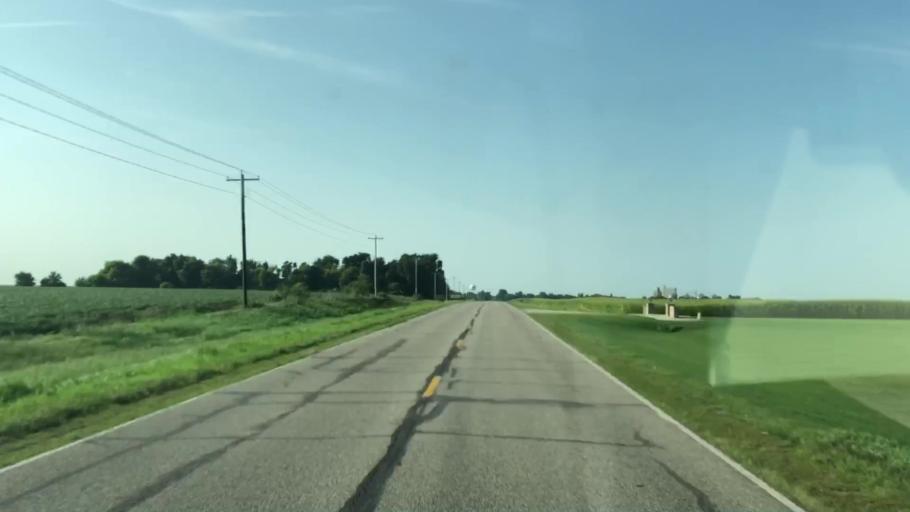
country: US
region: Iowa
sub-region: Lyon County
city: George
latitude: 43.3593
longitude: -95.9983
